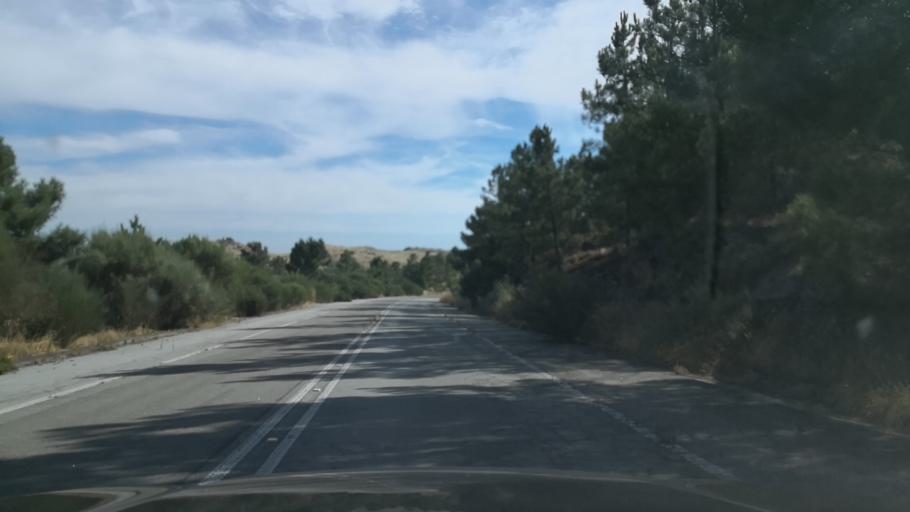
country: PT
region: Vila Real
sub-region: Sabrosa
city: Sabrosa
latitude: 41.3659
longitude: -7.5533
